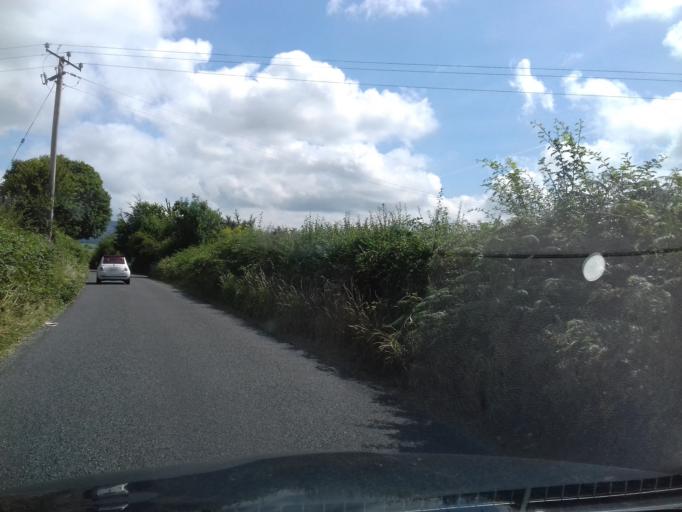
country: IE
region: Leinster
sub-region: Kilkenny
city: Graiguenamanagh
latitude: 52.6076
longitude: -6.8902
